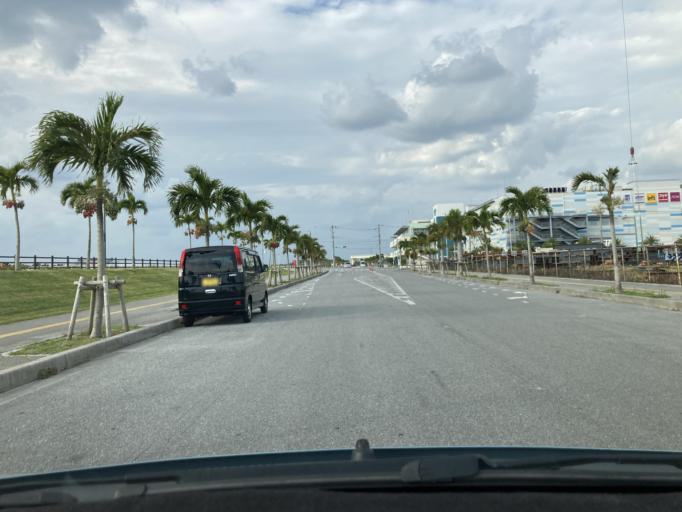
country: JP
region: Okinawa
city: Itoman
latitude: 26.1546
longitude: 127.6504
